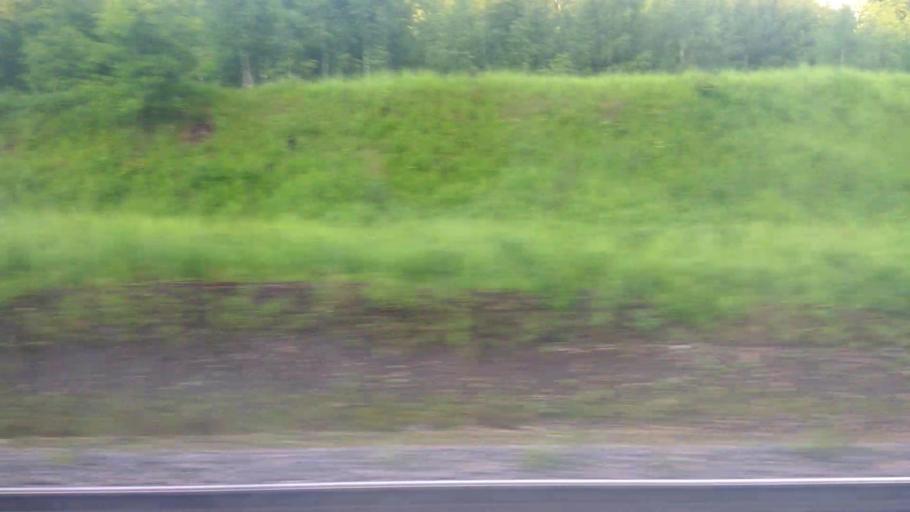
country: RU
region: Moskovskaya
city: Stupino
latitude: 54.9579
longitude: 38.0455
